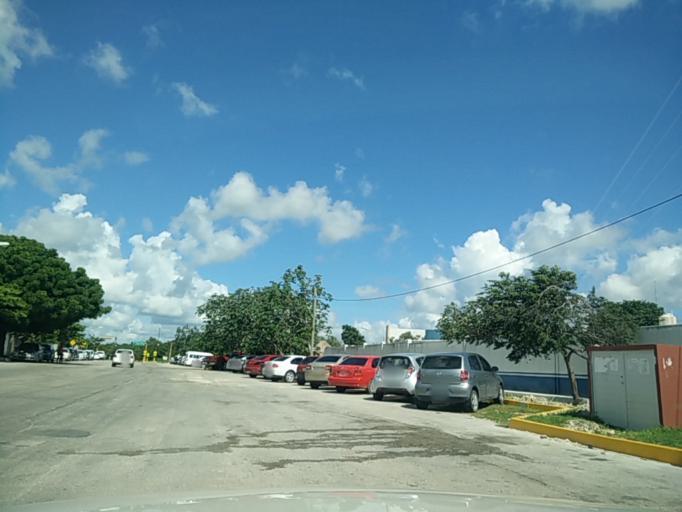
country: MX
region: Quintana Roo
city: Playa del Carmen
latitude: 20.6661
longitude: -87.0657
